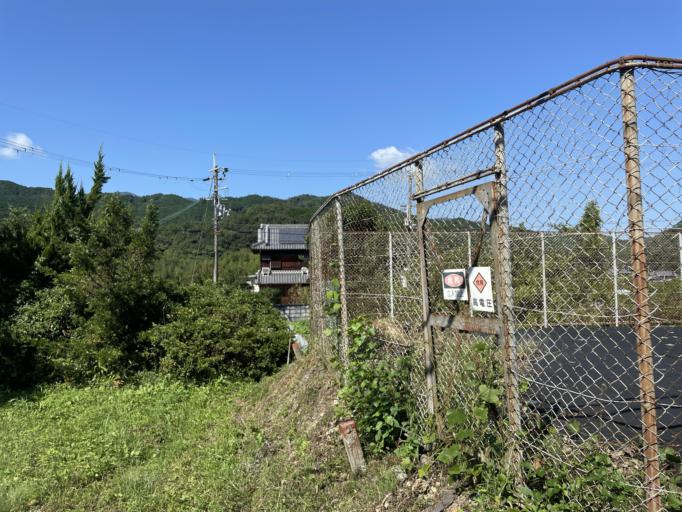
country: JP
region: Nara
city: Gose
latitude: 34.4109
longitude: 135.7460
